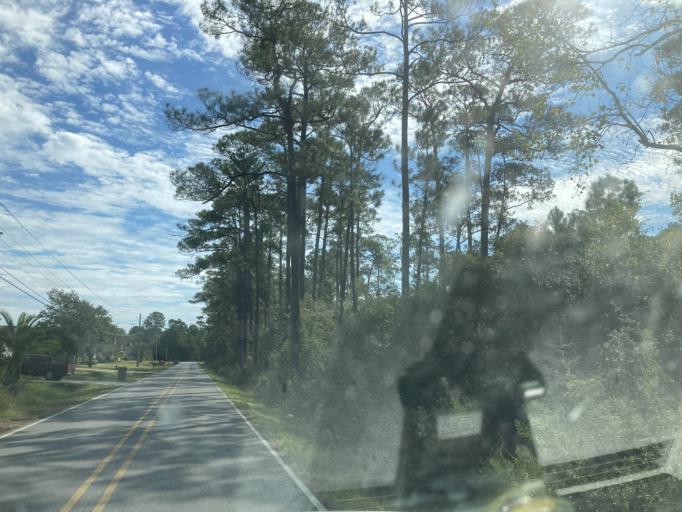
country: US
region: Mississippi
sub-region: Jackson County
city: Saint Martin
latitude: 30.4357
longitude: -88.8567
